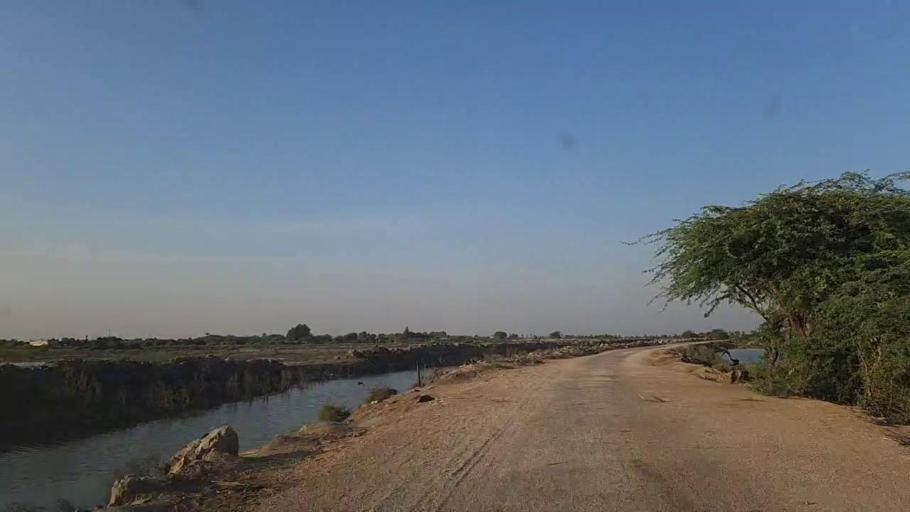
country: PK
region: Sindh
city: Mirpur Batoro
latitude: 24.6932
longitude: 68.2001
